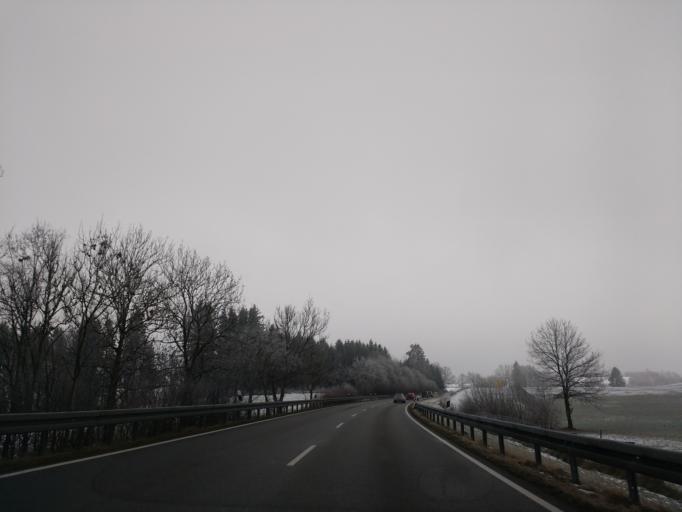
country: DE
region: Bavaria
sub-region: Swabia
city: Oy-Mittelberg
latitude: 47.6416
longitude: 10.4690
